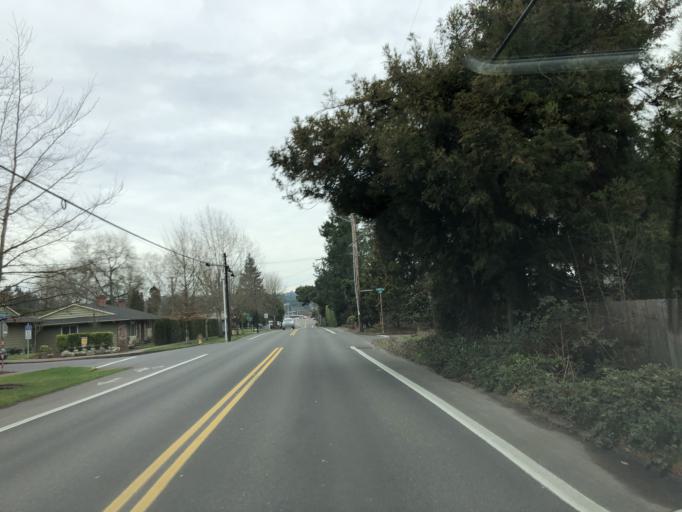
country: US
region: Oregon
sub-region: Washington County
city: Tigard
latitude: 45.4187
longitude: -122.7815
